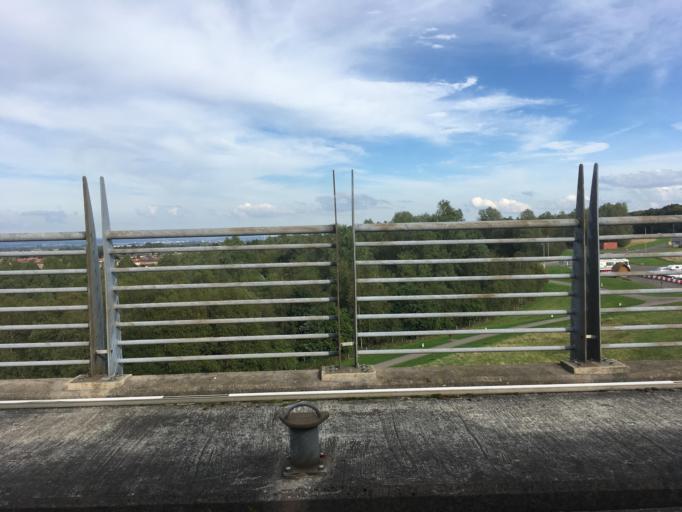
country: GB
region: Scotland
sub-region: Falkirk
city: Larbert
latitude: 55.9998
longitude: -3.8416
